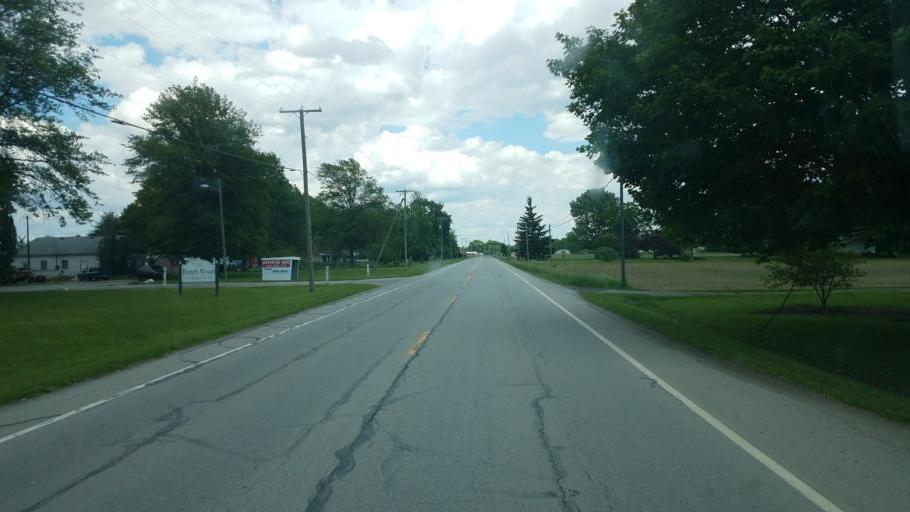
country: US
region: Ohio
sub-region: Crawford County
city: Galion
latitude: 40.8132
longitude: -82.8622
